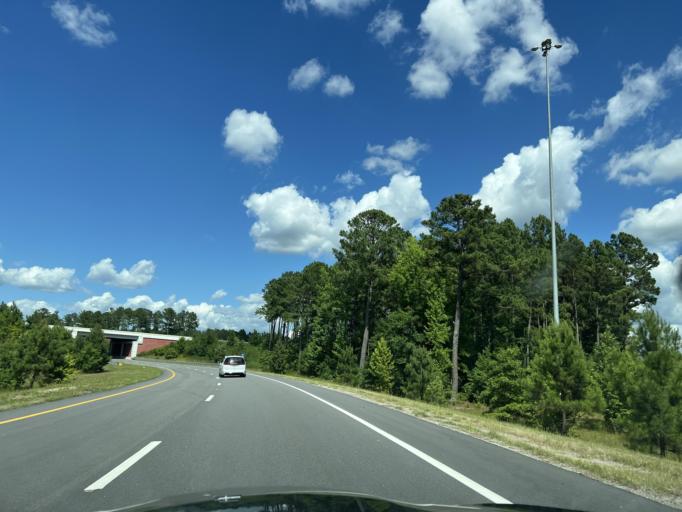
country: US
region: North Carolina
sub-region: Wake County
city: Apex
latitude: 35.6946
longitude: -78.8726
